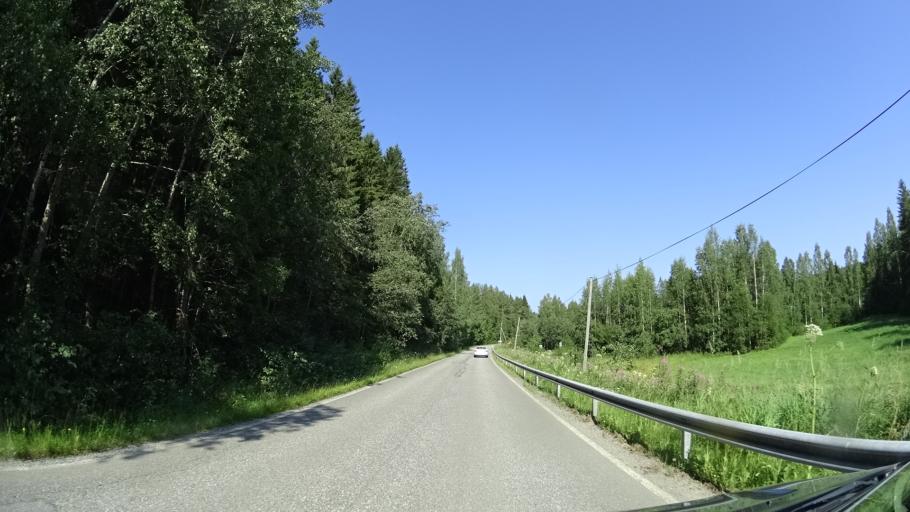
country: FI
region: North Karelia
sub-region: Pielisen Karjala
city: Lieksa
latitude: 63.1163
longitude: 29.7996
